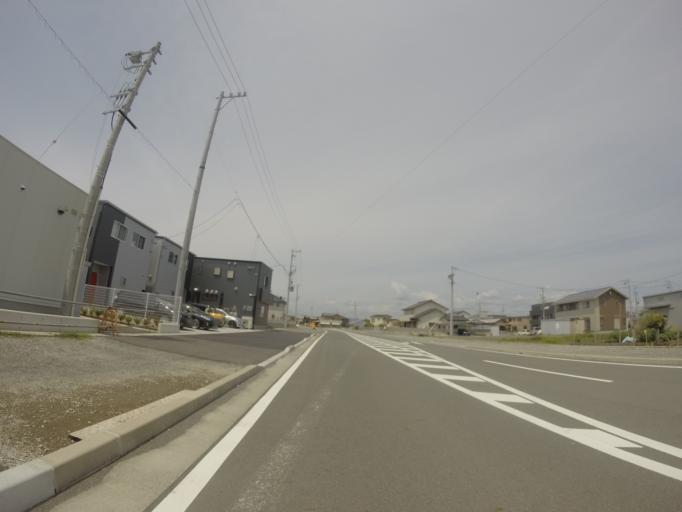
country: JP
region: Shizuoka
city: Yaizu
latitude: 34.8489
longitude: 138.3220
